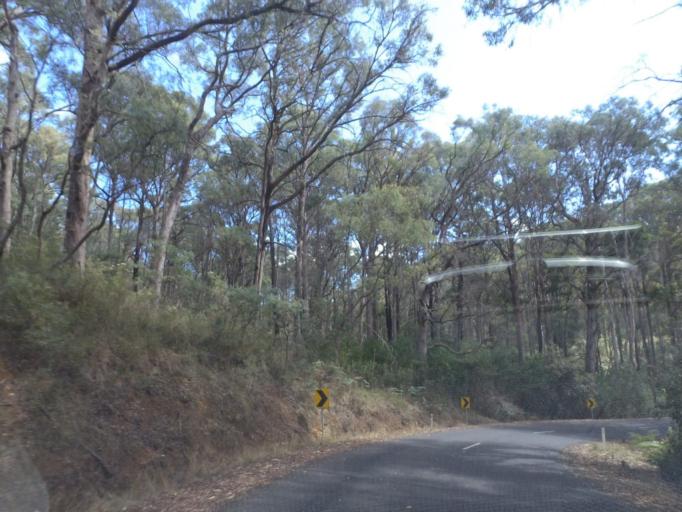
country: AU
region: Victoria
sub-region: Murrindindi
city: Alexandra
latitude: -37.3407
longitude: 145.9631
